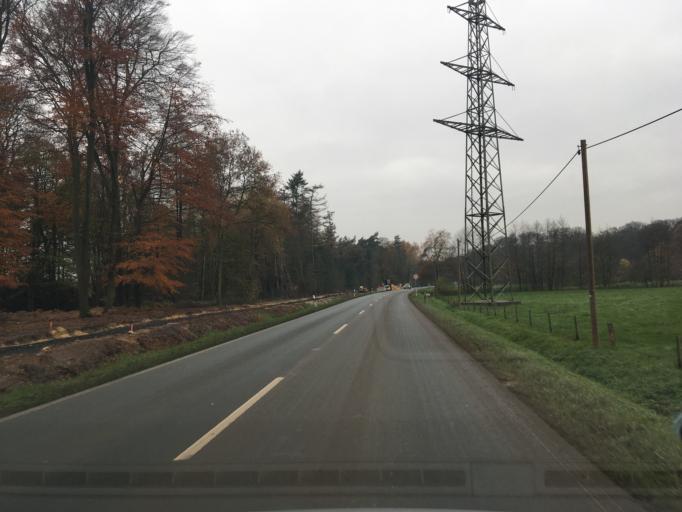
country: DE
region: North Rhine-Westphalia
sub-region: Regierungsbezirk Munster
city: Legden
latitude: 52.0281
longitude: 7.0793
